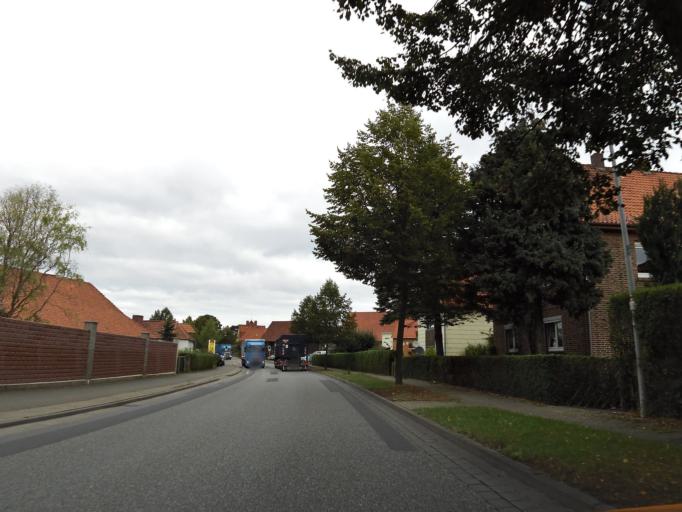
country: DE
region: Lower Saxony
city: Northeim
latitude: 51.7652
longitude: 9.9590
